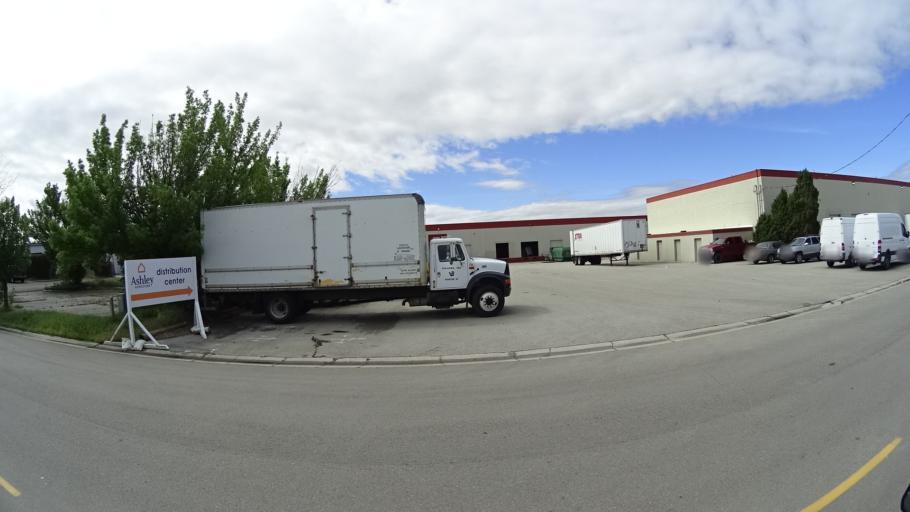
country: US
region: Idaho
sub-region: Ada County
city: Boise
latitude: 43.5604
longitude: -116.1915
